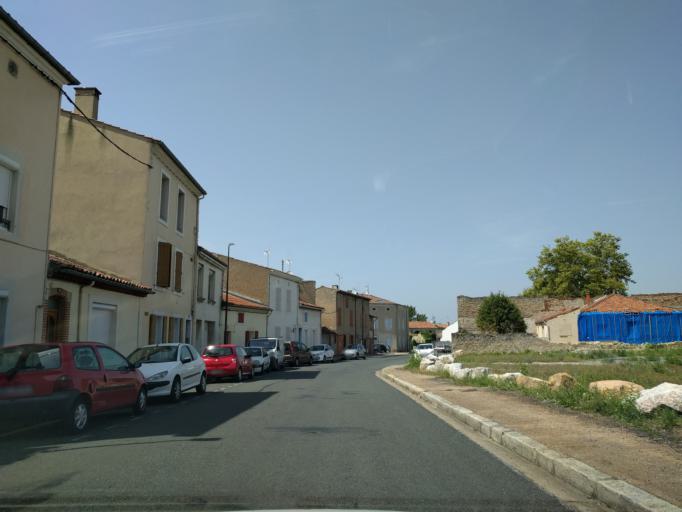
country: FR
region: Midi-Pyrenees
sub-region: Departement du Tarn
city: Castres
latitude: 43.5986
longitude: 2.2439
